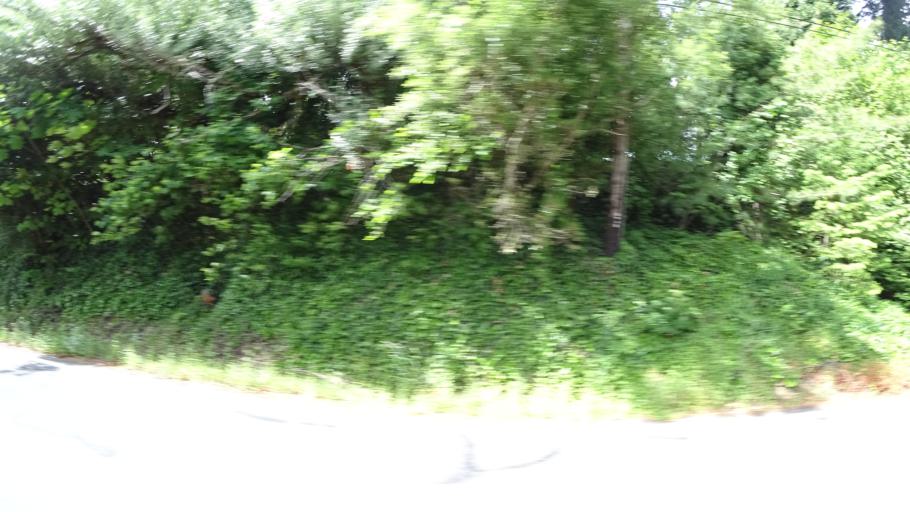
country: US
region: Oregon
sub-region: Washington County
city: Bethany
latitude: 45.5997
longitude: -122.8288
